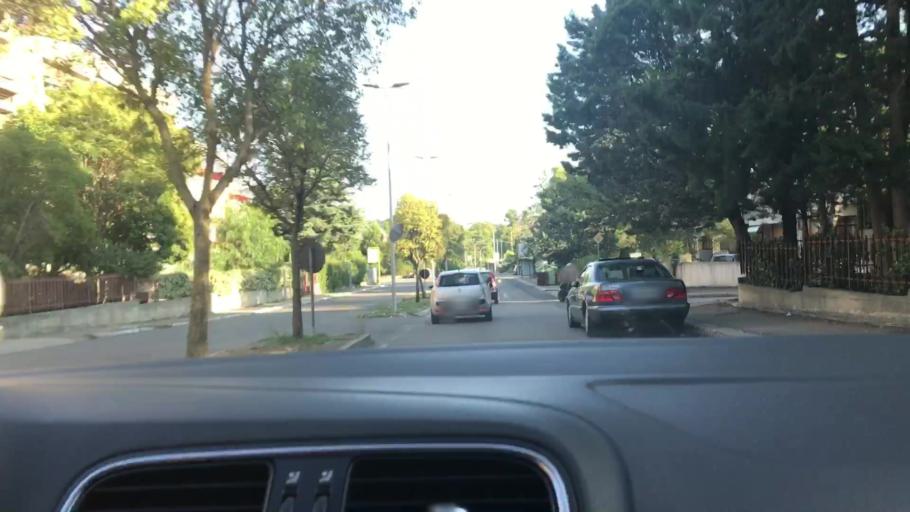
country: IT
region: Basilicate
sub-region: Provincia di Matera
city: Matera
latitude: 40.6820
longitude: 16.5865
